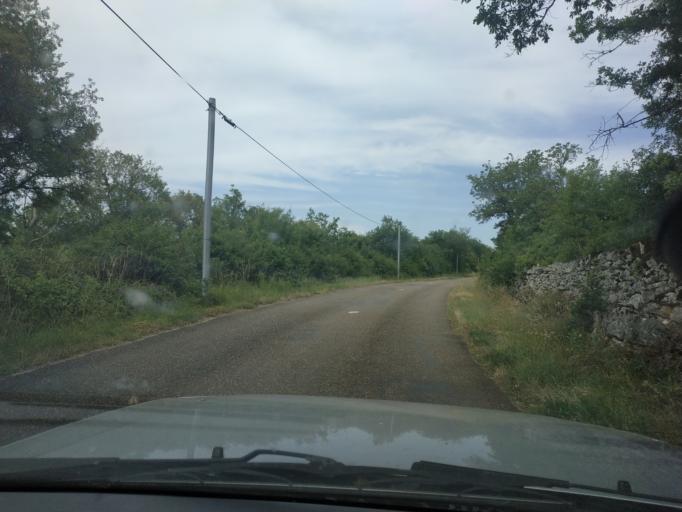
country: FR
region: Midi-Pyrenees
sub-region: Departement du Lot
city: Gramat
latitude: 44.6013
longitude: 1.6653
